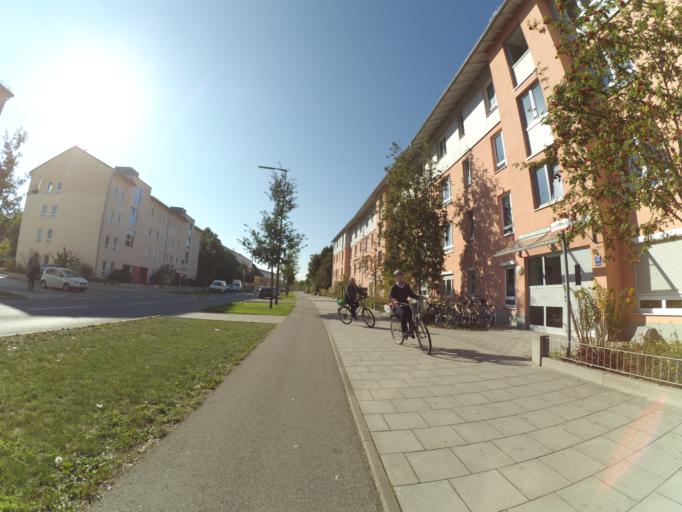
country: DE
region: Bavaria
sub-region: Upper Bavaria
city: Oberschleissheim
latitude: 48.2037
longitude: 11.5730
